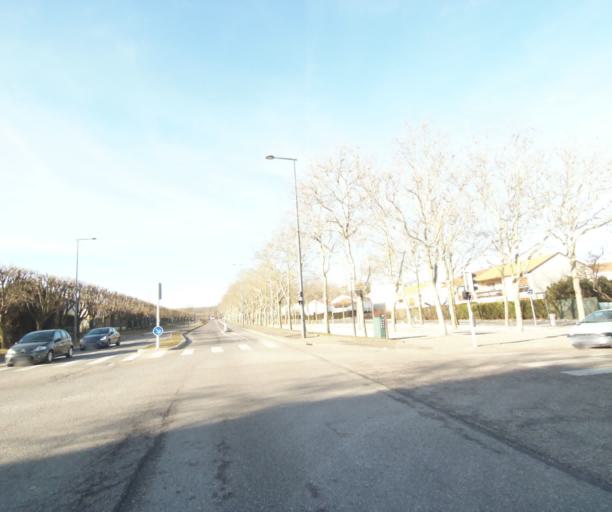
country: FR
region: Lorraine
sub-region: Departement de Meurthe-et-Moselle
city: Chavigny
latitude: 48.6572
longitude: 6.1119
